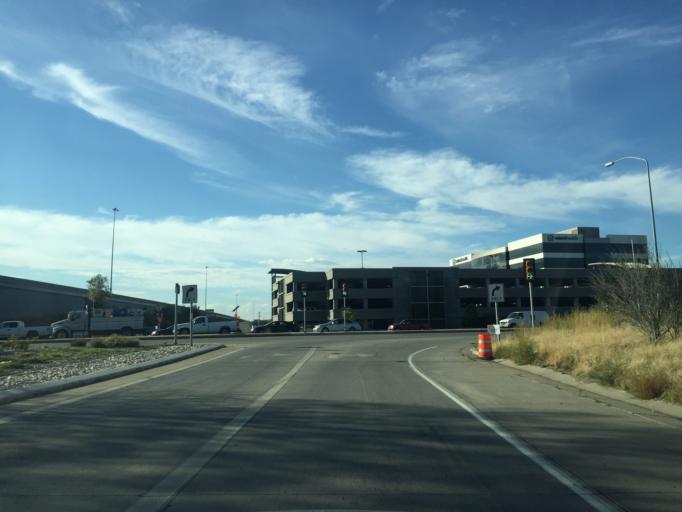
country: US
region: Utah
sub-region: Salt Lake County
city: Murray
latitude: 40.6552
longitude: -111.9025
